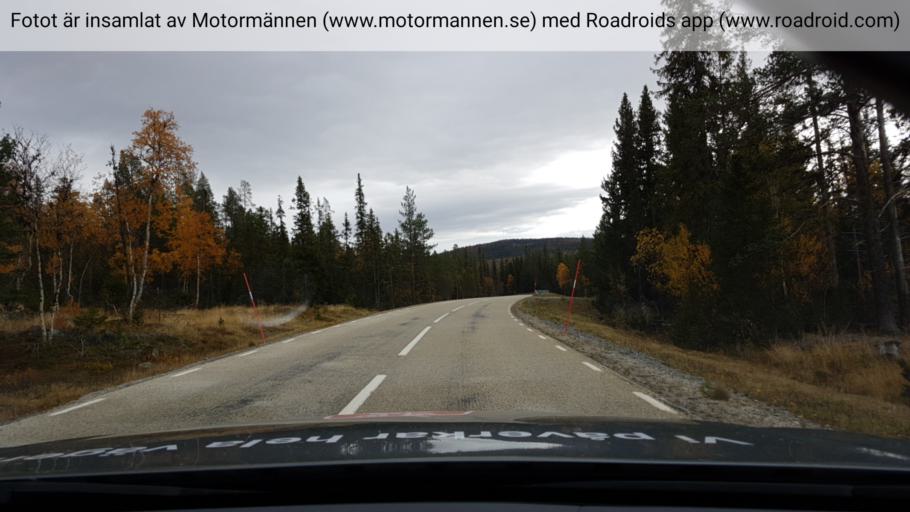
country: SE
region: Jaemtland
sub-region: Are Kommun
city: Are
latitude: 62.8388
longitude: 12.8364
